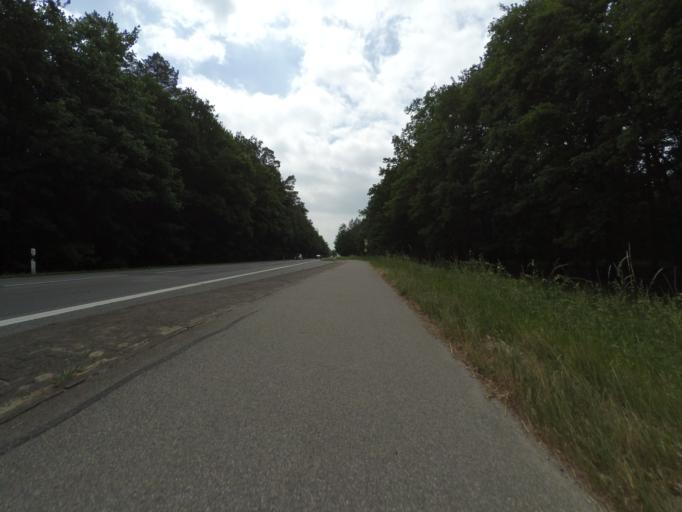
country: DE
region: Mecklenburg-Vorpommern
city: Klink
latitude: 53.4932
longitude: 12.6292
